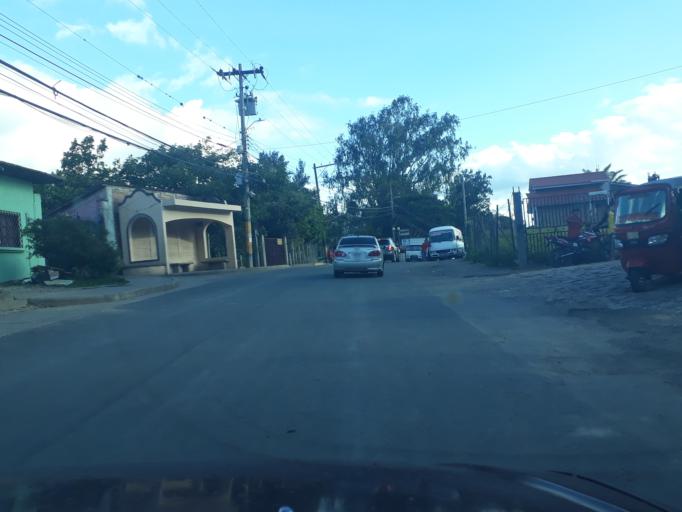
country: HN
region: Francisco Morazan
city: El Chimbo
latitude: 14.1176
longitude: -87.1126
